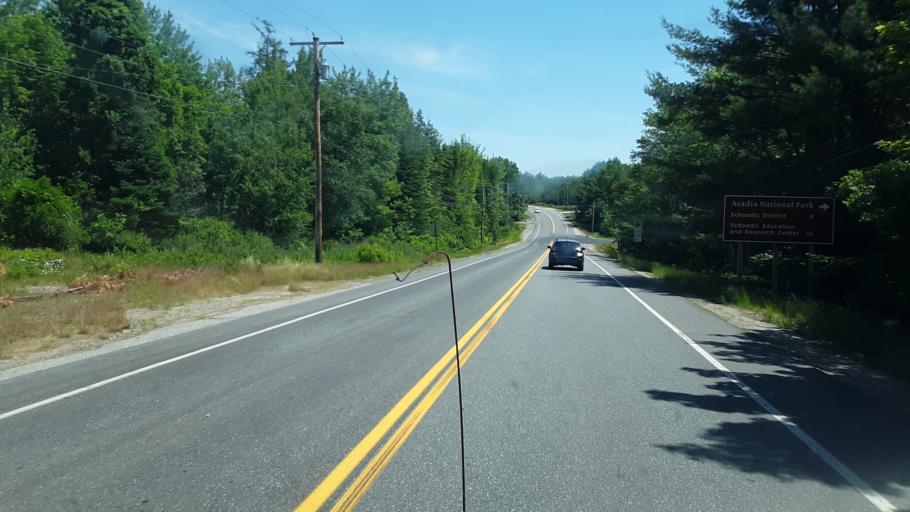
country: US
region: Maine
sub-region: Hancock County
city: Gouldsboro
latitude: 44.4751
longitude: -68.0989
